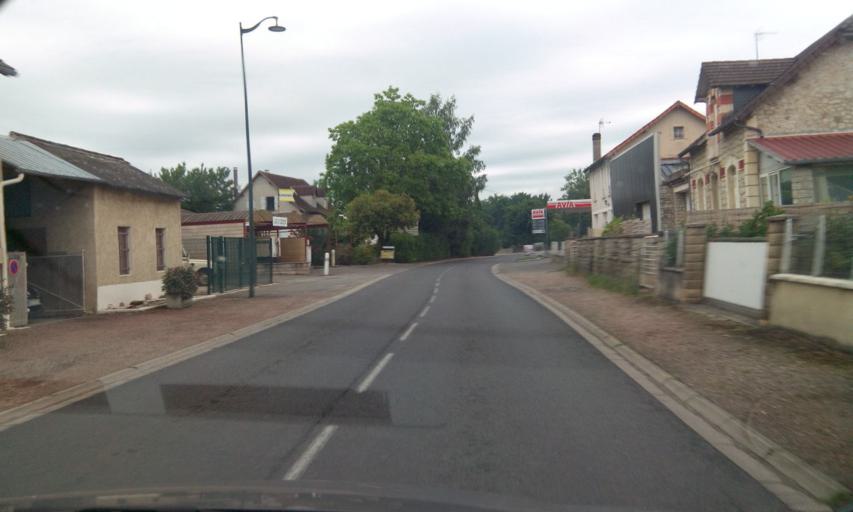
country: FR
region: Midi-Pyrenees
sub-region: Departement du Lot
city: Vayrac
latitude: 44.9536
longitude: 1.7096
